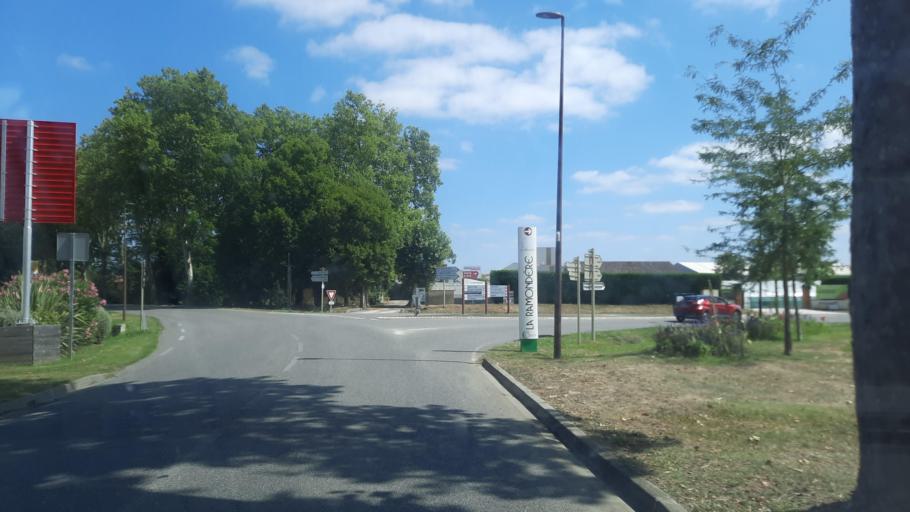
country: FR
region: Midi-Pyrenees
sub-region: Departement du Gers
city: Lombez
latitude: 43.4743
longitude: 0.9158
